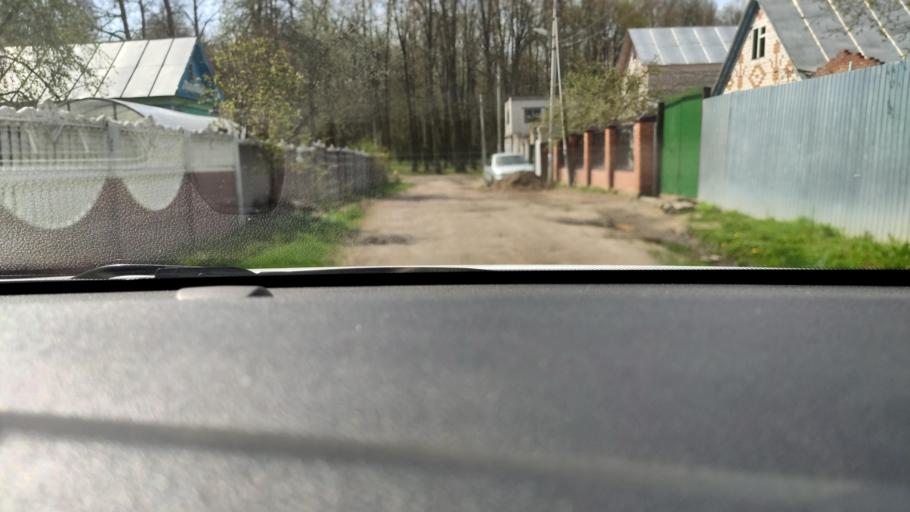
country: RU
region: Tatarstan
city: Osinovo
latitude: 55.8486
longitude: 48.8844
